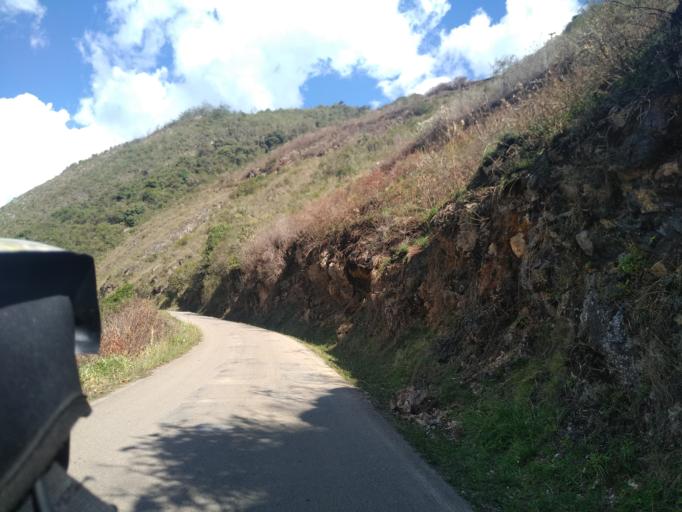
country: PE
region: Amazonas
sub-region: Provincia de Chachapoyas
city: Montevideo
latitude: -6.7138
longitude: -77.8170
